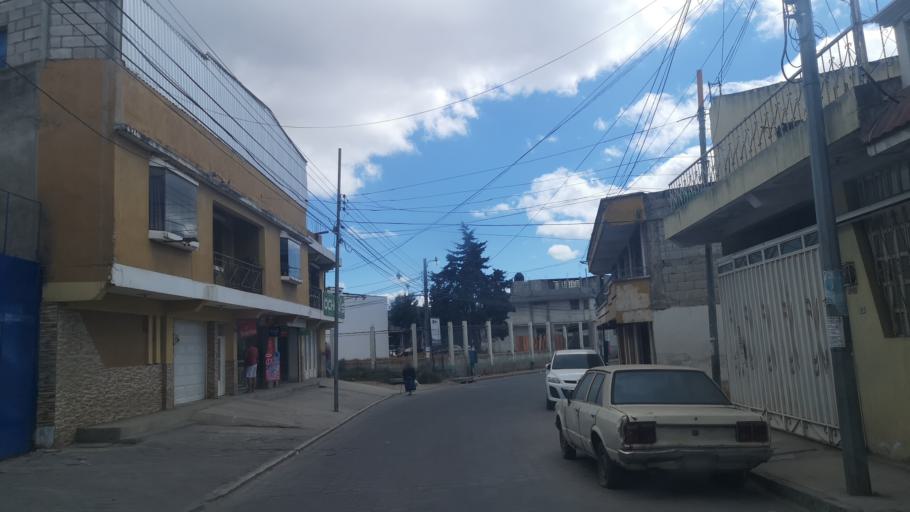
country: GT
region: Quetzaltenango
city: Quetzaltenango
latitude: 14.8374
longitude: -91.5368
